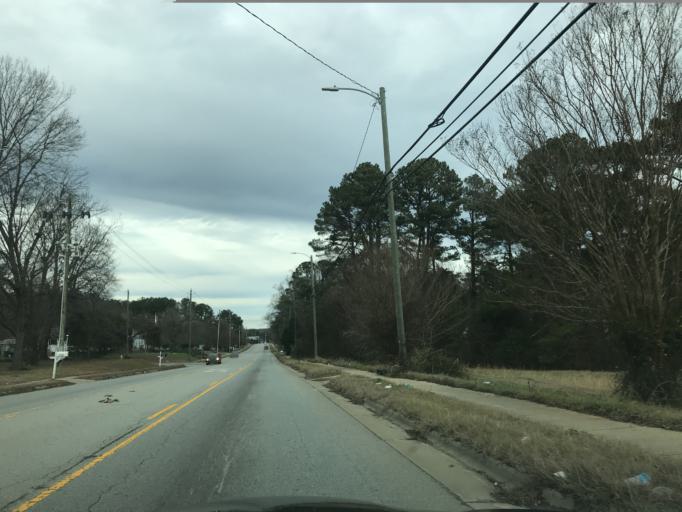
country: US
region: North Carolina
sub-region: Wake County
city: Raleigh
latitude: 35.7431
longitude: -78.6310
